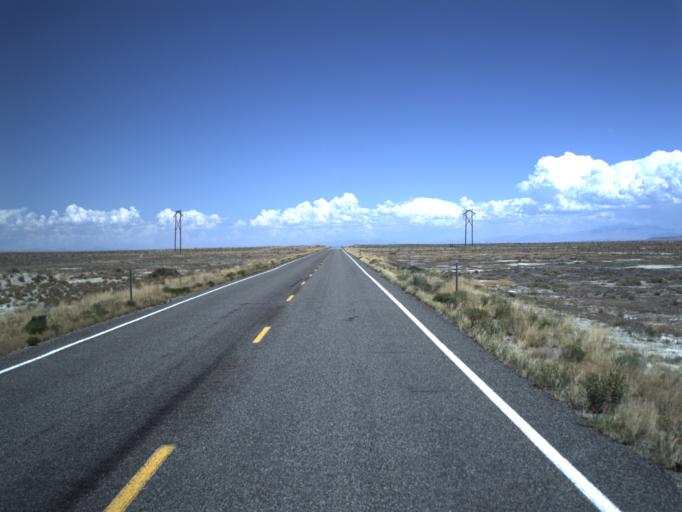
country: US
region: Utah
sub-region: Millard County
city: Delta
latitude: 39.1704
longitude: -113.0347
